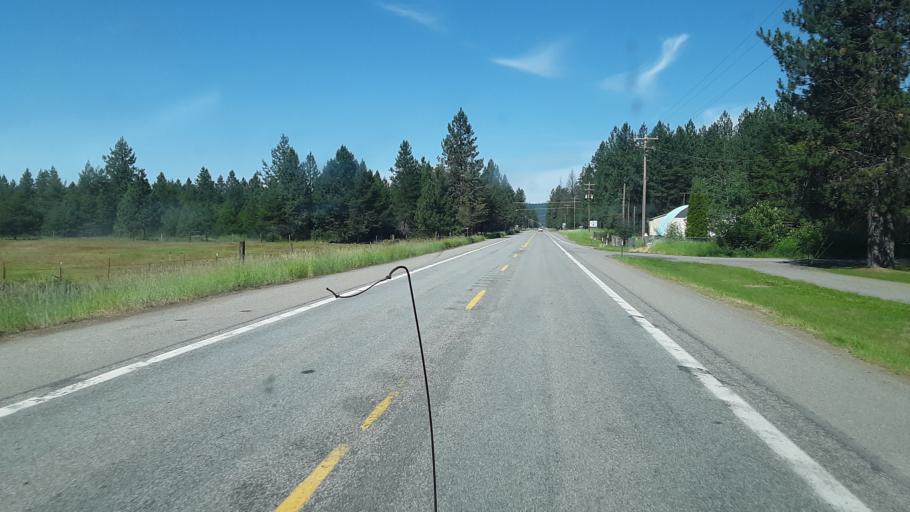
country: US
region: Idaho
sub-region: Kootenai County
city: Hayden
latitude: 47.8173
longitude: -116.8245
